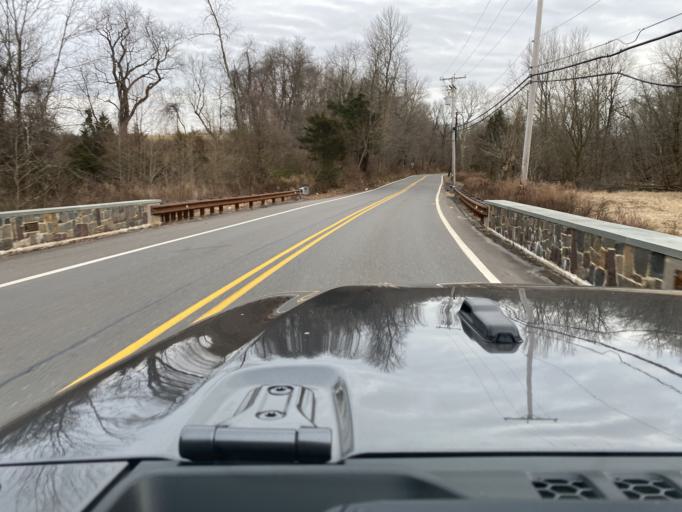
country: US
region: New Jersey
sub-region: Somerset County
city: Bloomingdale
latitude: 40.5049
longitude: -74.7231
